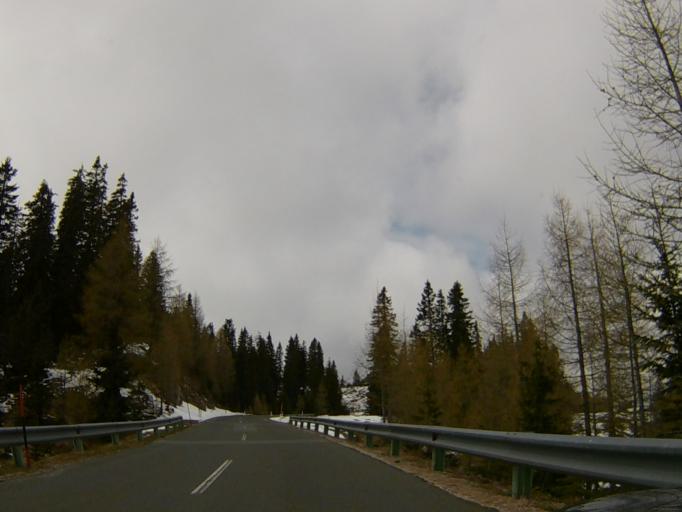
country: AT
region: Carinthia
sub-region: Politischer Bezirk Villach Land
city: Arnoldstein
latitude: 46.5953
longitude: 13.7172
